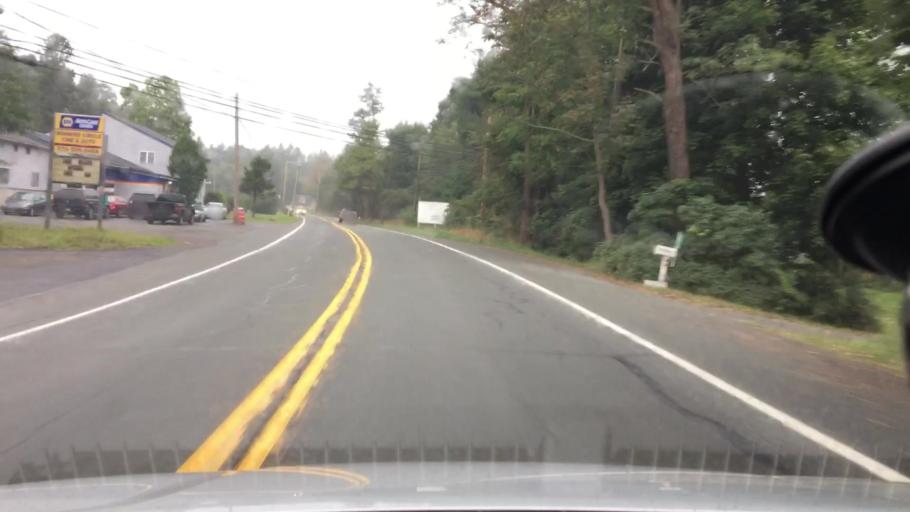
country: US
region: Pennsylvania
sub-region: Monroe County
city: Mountainhome
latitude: 41.1589
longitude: -75.2793
